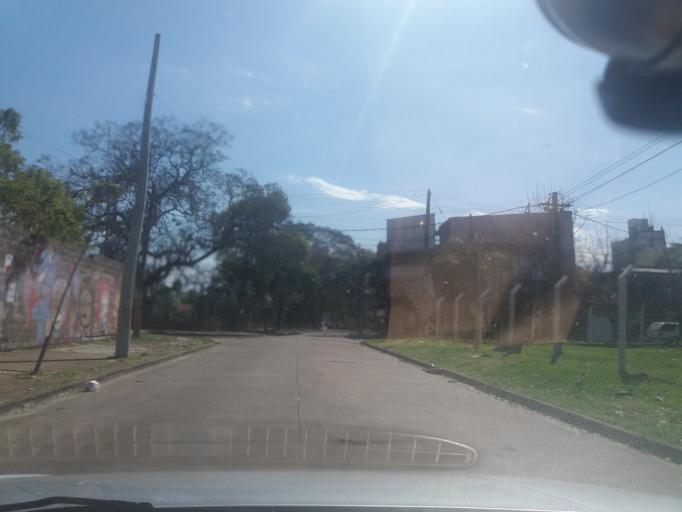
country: AR
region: Corrientes
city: Corrientes
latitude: -27.4702
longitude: -58.8510
